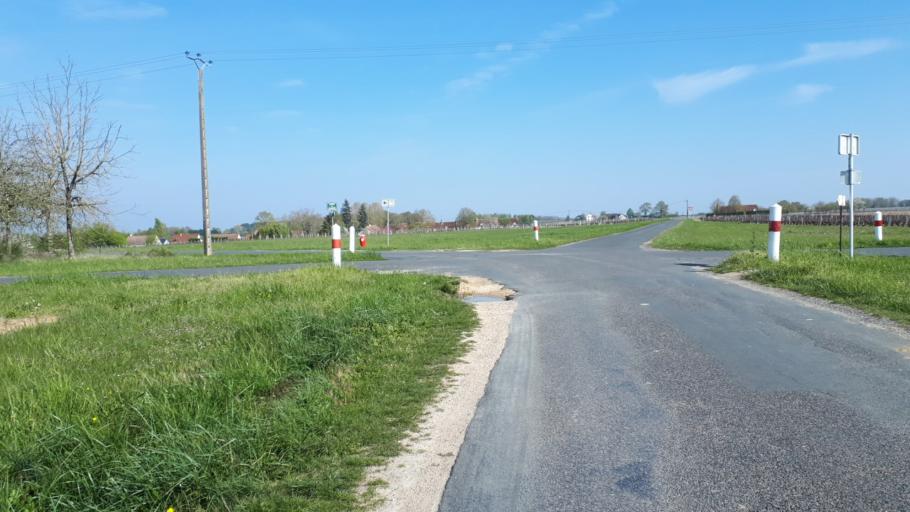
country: FR
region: Centre
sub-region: Departement du Loir-et-Cher
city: Contres
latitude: 47.3877
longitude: 1.3861
